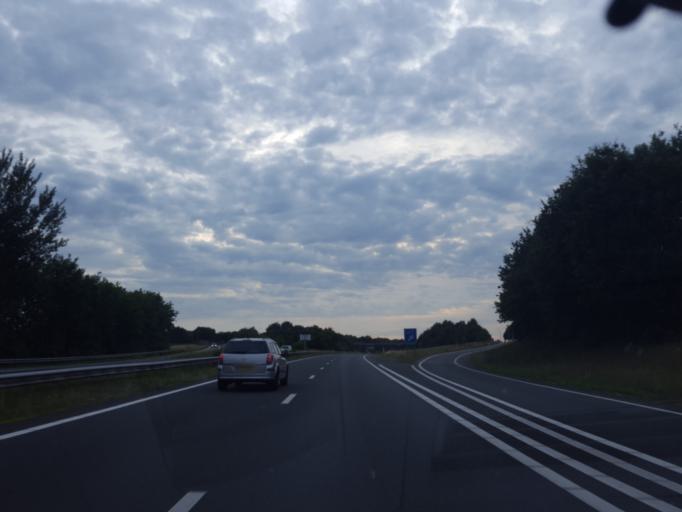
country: NL
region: Overijssel
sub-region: Gemeente Steenwijkerland
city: Tuk
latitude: 52.8046
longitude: 6.1004
